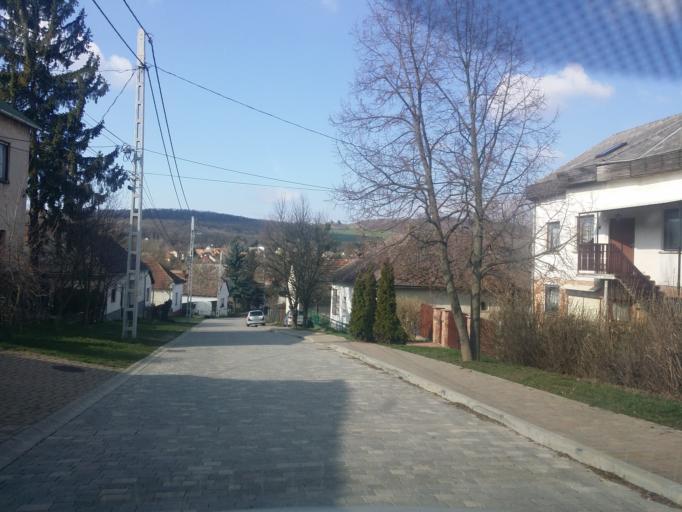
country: HU
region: Fejer
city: Many
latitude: 47.5914
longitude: 18.6467
